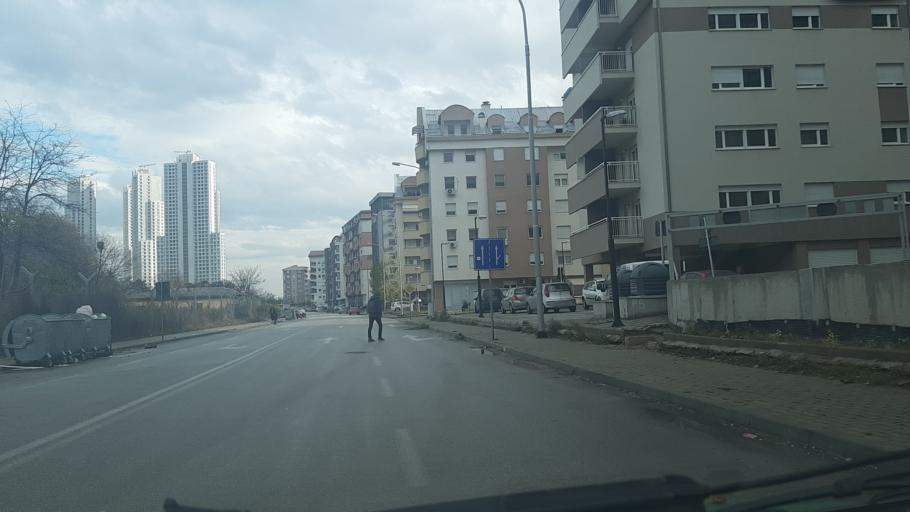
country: MK
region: Kisela Voda
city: Usje
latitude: 41.9817
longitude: 21.4572
